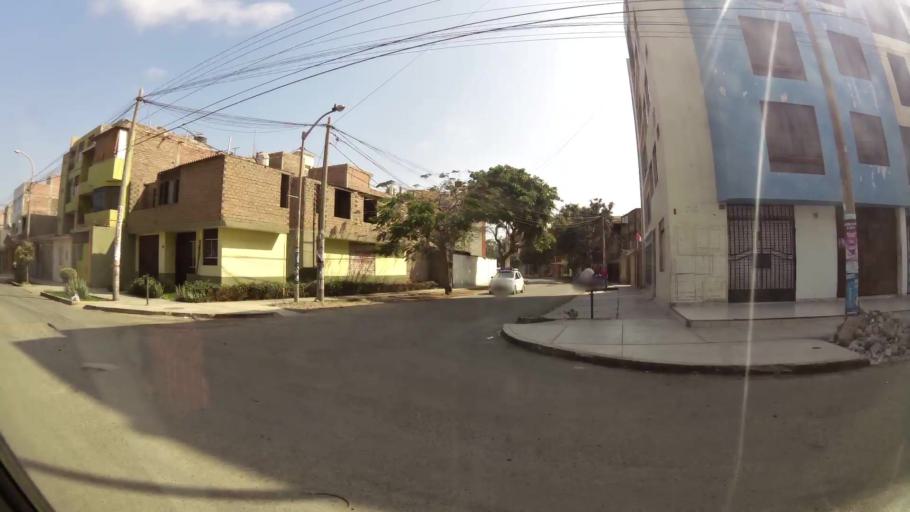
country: PE
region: La Libertad
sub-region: Provincia de Trujillo
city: Trujillo
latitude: -8.1253
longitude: -79.0176
